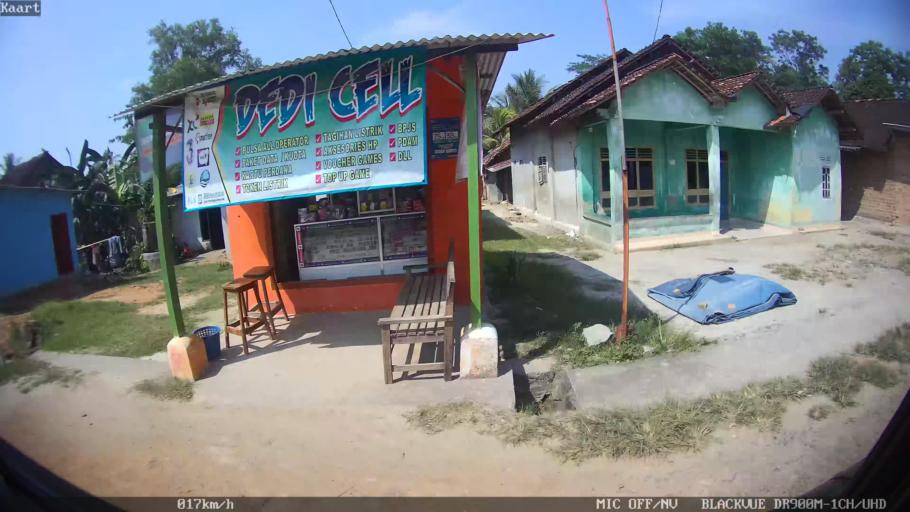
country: ID
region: Lampung
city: Natar
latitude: -5.2532
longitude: 105.1959
